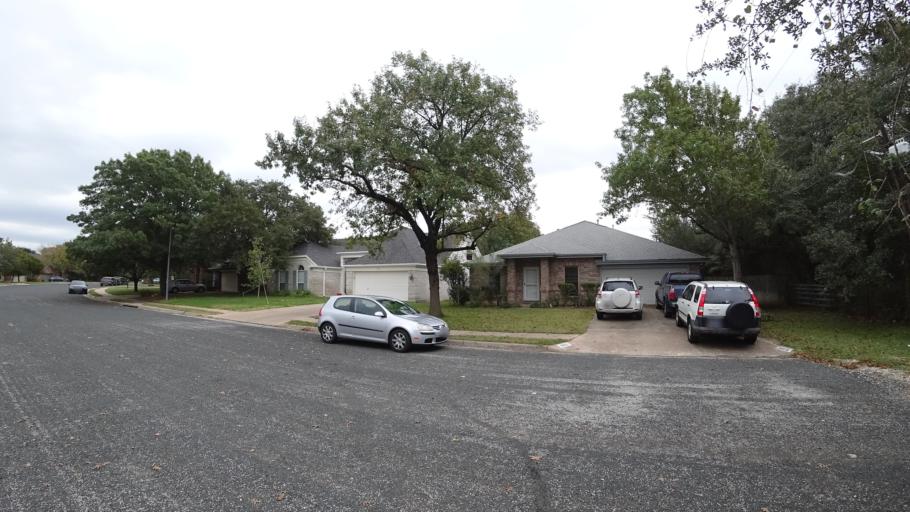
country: US
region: Texas
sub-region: Williamson County
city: Brushy Creek
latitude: 30.5023
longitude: -97.7451
